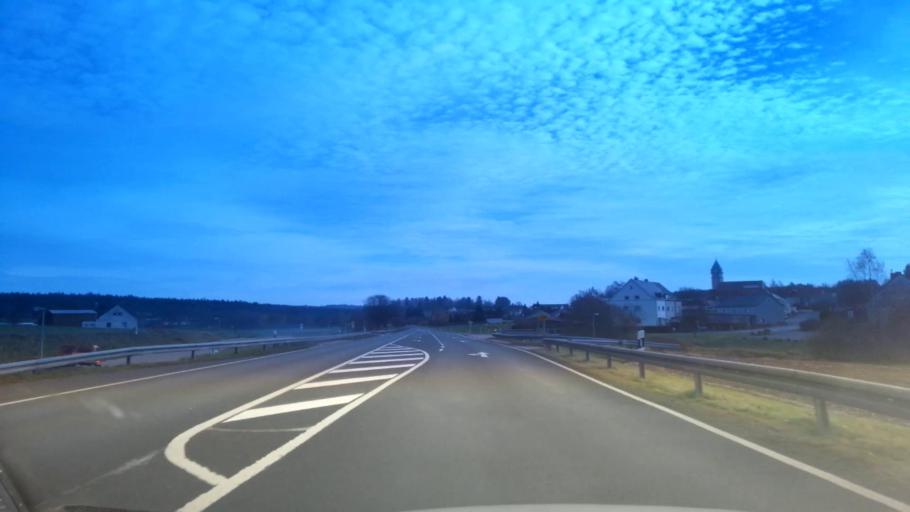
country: DE
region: Bavaria
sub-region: Upper Palatinate
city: Pechbrunn
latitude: 49.9738
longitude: 12.1628
